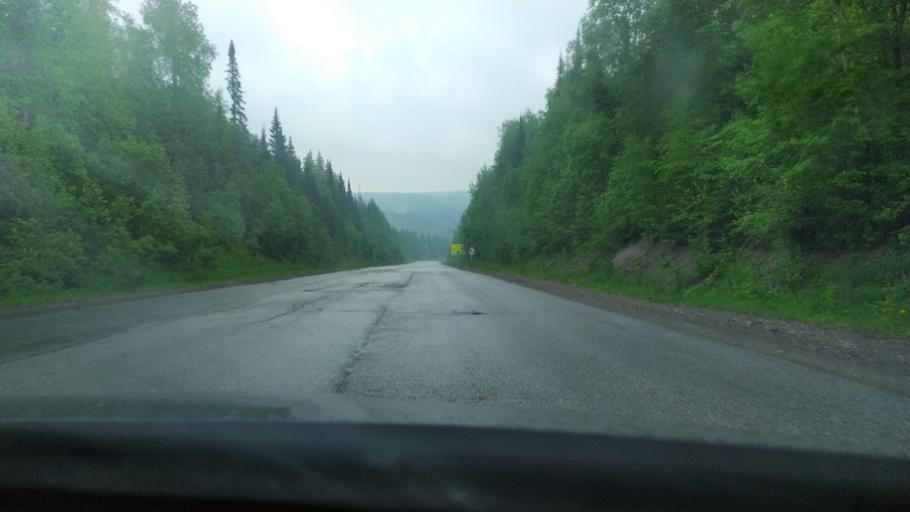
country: RU
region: Perm
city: Gremyachinsk
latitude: 58.4507
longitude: 57.8719
